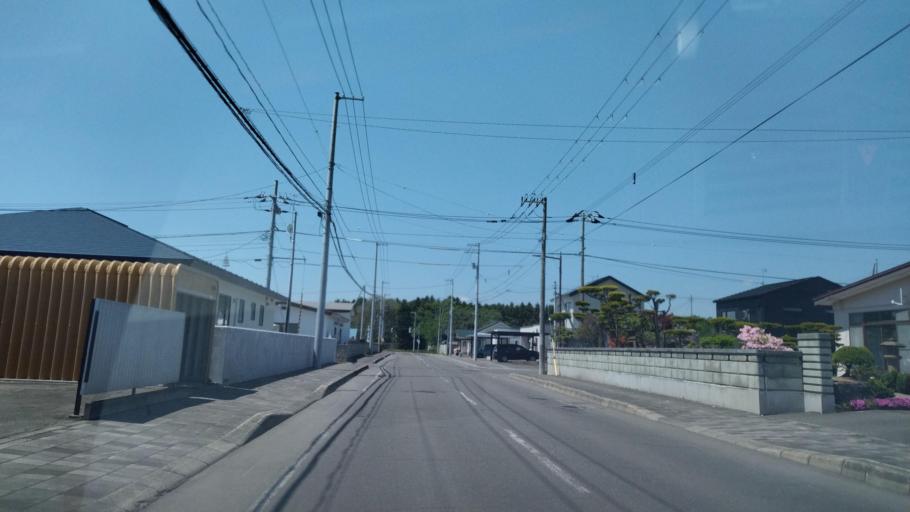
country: JP
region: Hokkaido
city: Otofuke
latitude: 43.1649
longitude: 143.2442
